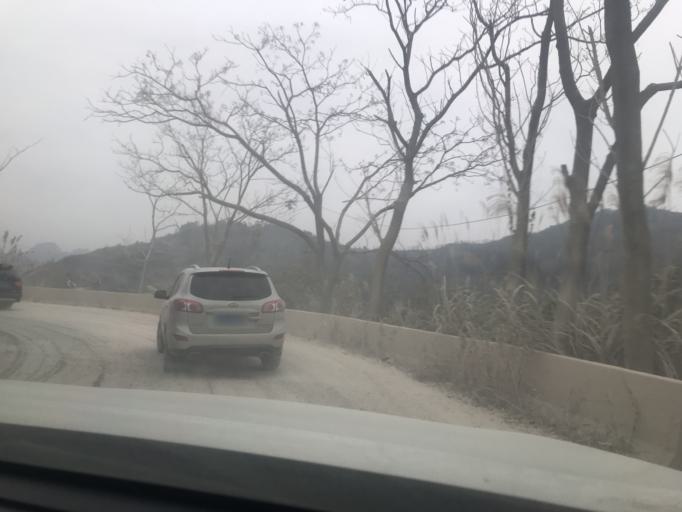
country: CN
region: Guangxi Zhuangzu Zizhiqu
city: Xinzhou
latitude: 25.0062
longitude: 105.8356
